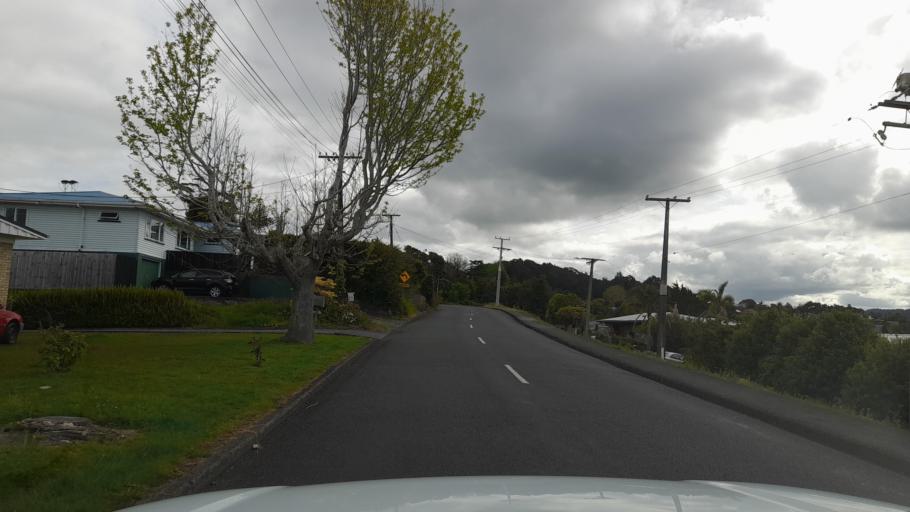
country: NZ
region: Northland
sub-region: Whangarei
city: Whangarei
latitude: -35.7386
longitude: 174.3227
